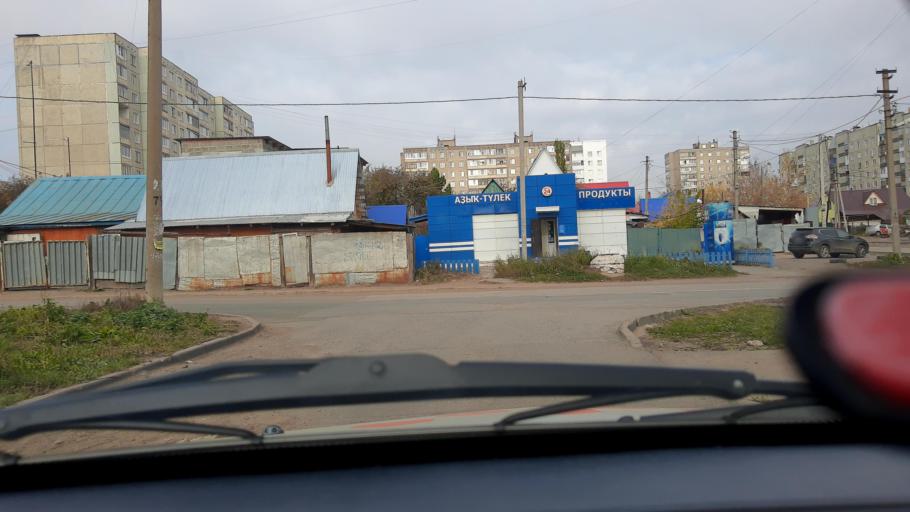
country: RU
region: Bashkortostan
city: Ufa
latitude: 54.8173
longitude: 56.1300
